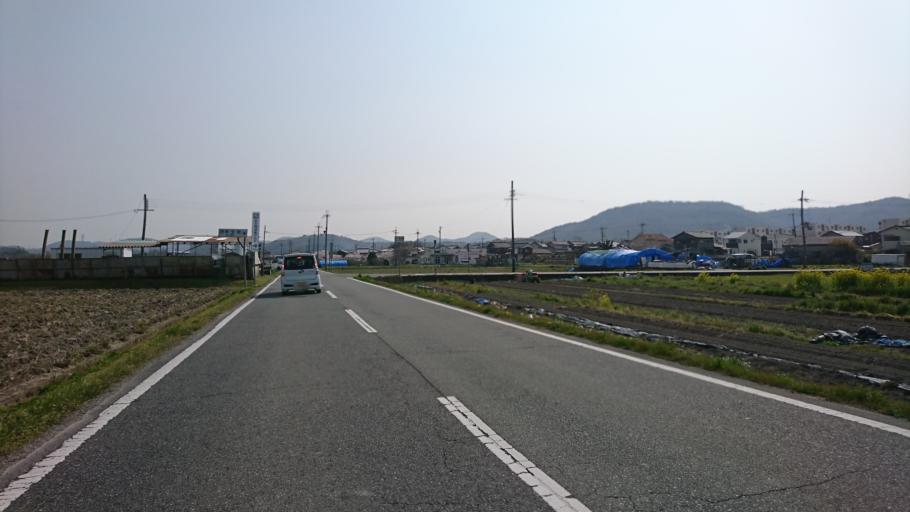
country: JP
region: Hyogo
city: Ono
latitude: 34.8569
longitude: 134.9119
